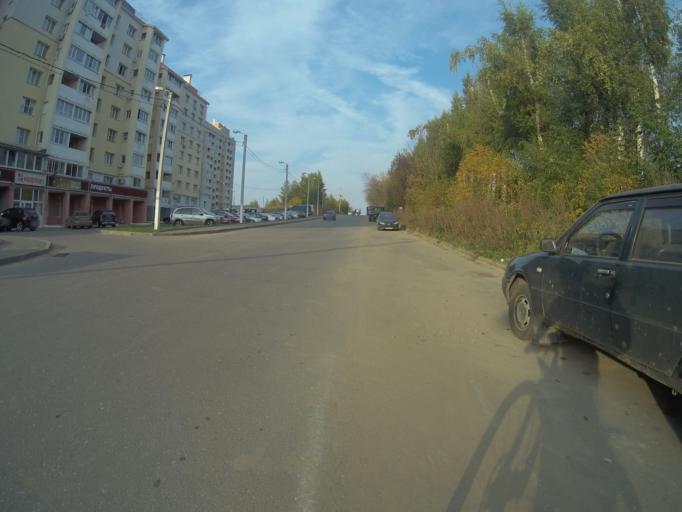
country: RU
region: Vladimir
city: Vladimir
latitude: 56.1590
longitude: 40.3742
